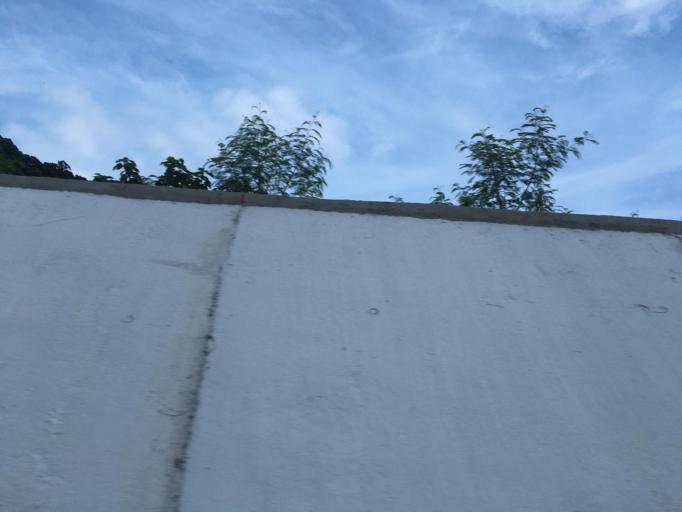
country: TW
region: Taiwan
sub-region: Yilan
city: Yilan
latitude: 24.4472
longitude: 121.7792
